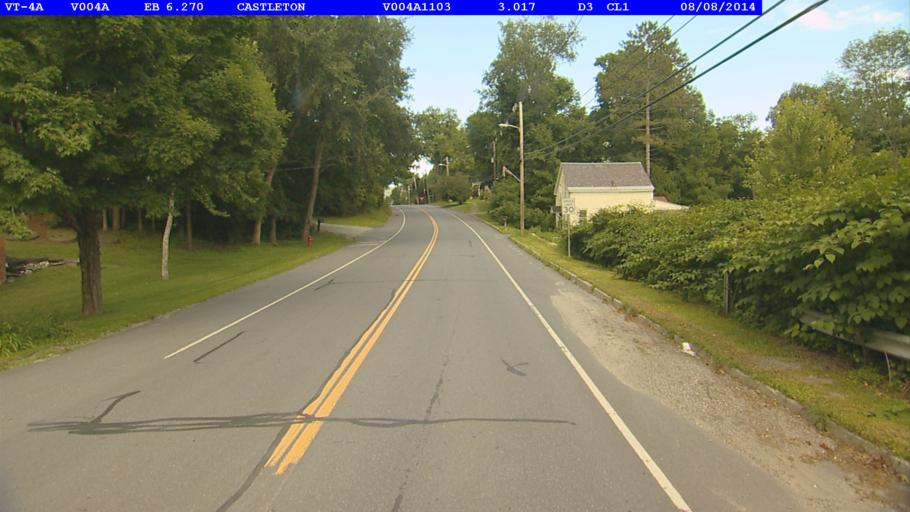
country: US
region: Vermont
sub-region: Rutland County
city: Castleton
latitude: 43.6101
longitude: -73.1848
